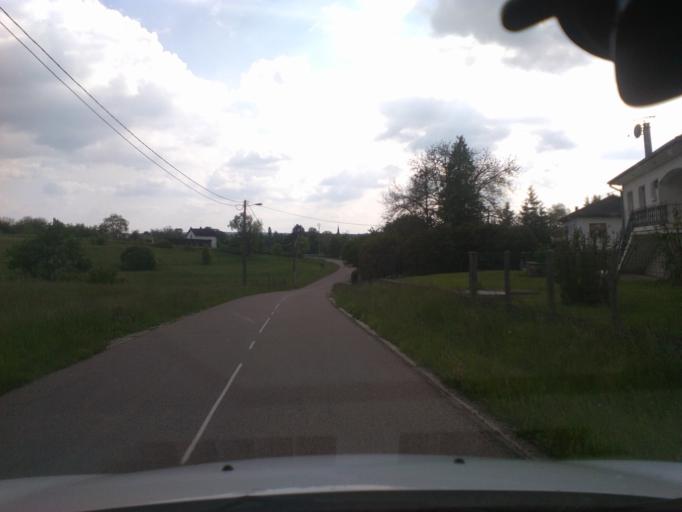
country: FR
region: Lorraine
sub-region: Departement des Vosges
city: Mirecourt
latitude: 48.3082
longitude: 6.1459
